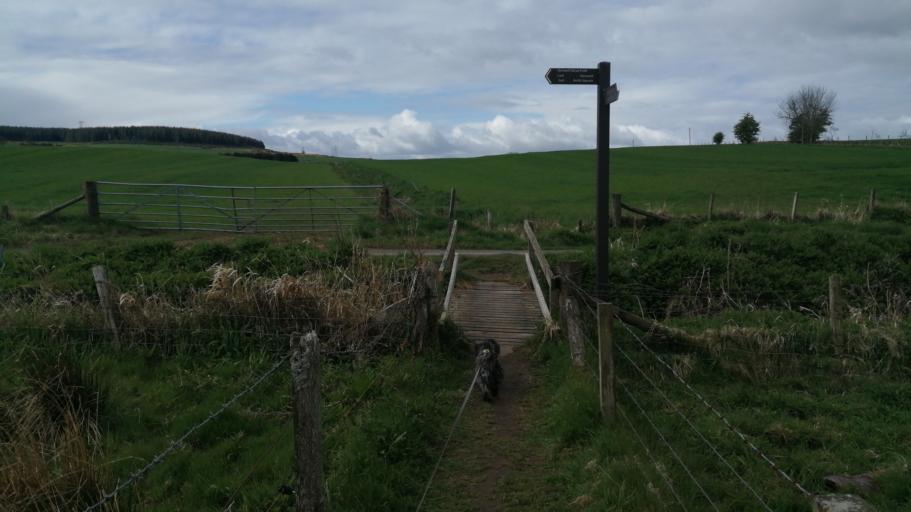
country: GB
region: Scotland
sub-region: Moray
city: Keith
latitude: 57.5305
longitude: -2.9621
